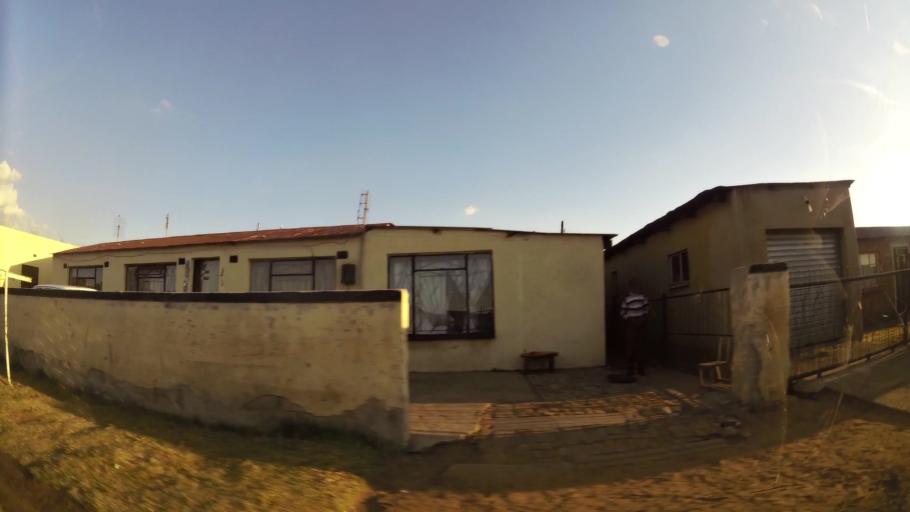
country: ZA
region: Mpumalanga
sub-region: Nkangala District Municipality
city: Witbank
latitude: -25.8812
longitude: 29.1977
